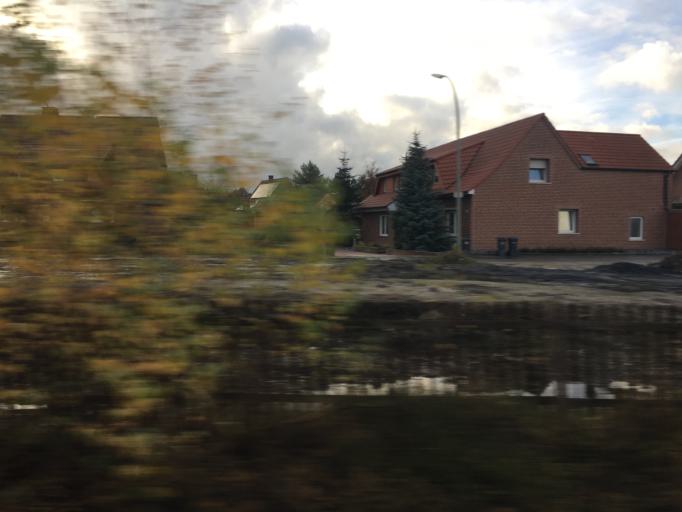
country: DE
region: North Rhine-Westphalia
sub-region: Regierungsbezirk Munster
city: Altenberge
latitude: 52.0547
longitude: 7.4793
